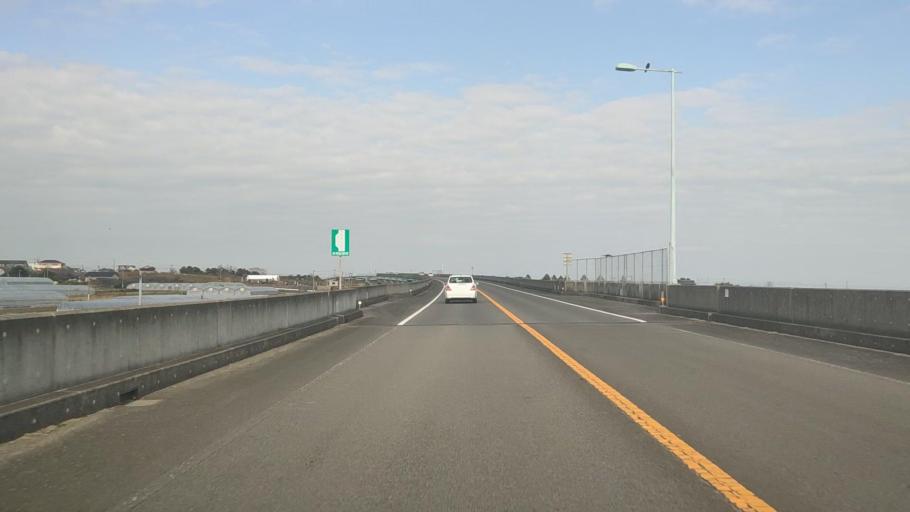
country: JP
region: Nagasaki
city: Shimabara
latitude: 32.7346
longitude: 130.3690
